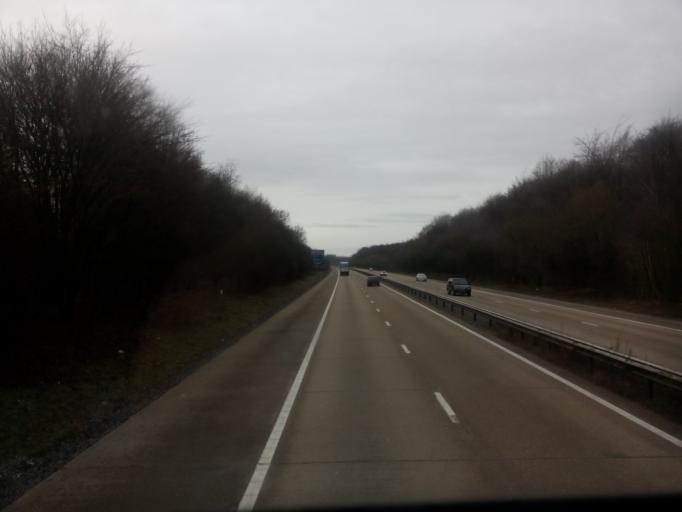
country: GB
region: England
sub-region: Hampshire
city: Kings Worthy
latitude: 51.1447
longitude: -1.2433
